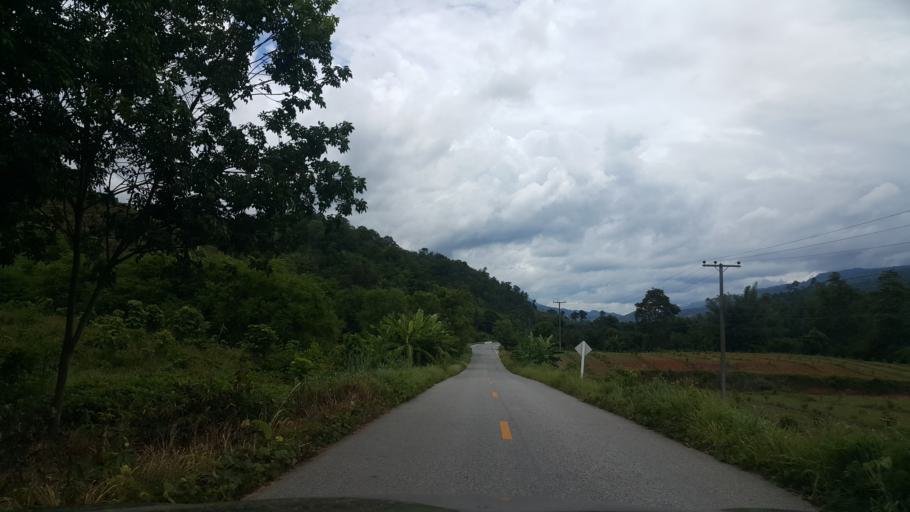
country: TH
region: Phitsanulok
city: Chat Trakan
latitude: 17.4012
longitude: 100.7622
